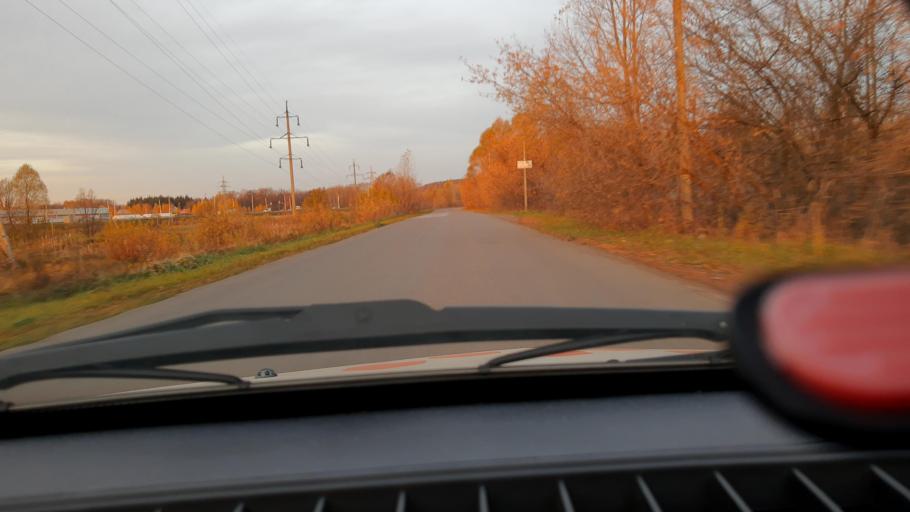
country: RU
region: Bashkortostan
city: Ufa
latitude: 54.8082
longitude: 56.1792
